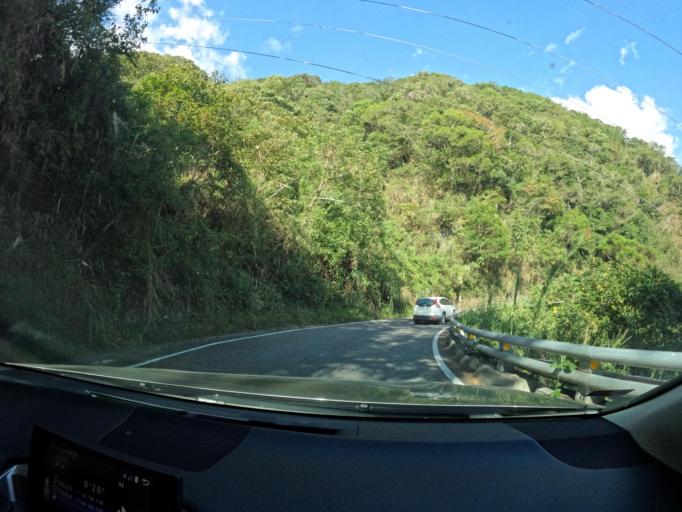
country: TW
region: Taiwan
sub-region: Taitung
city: Taitung
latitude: 23.1907
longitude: 121.0191
